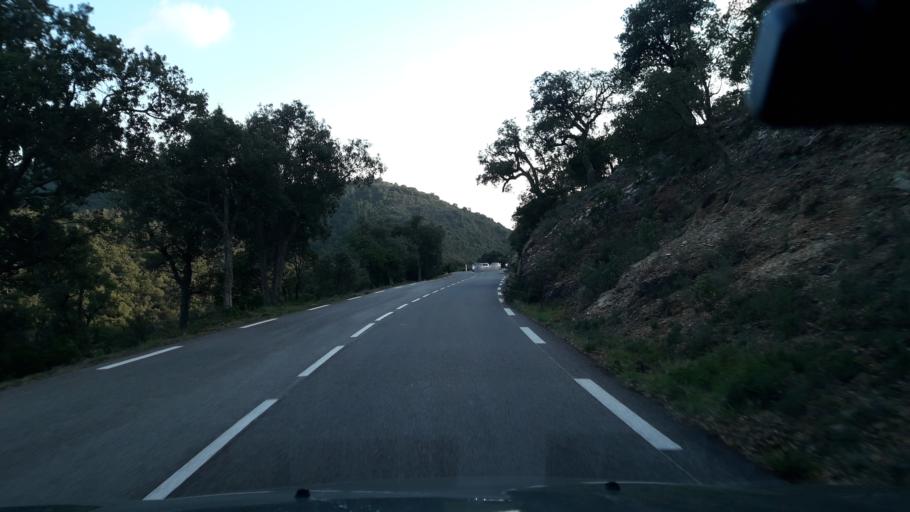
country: FR
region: Provence-Alpes-Cote d'Azur
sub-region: Departement du Var
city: Saint-Raphael
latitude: 43.4992
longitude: 6.7819
